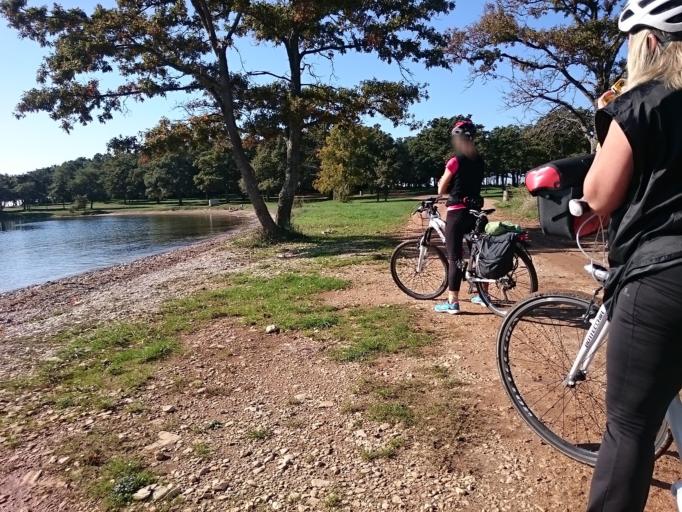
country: HR
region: Istarska
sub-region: Grad Porec
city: Porec
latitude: 45.2659
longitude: 13.5763
